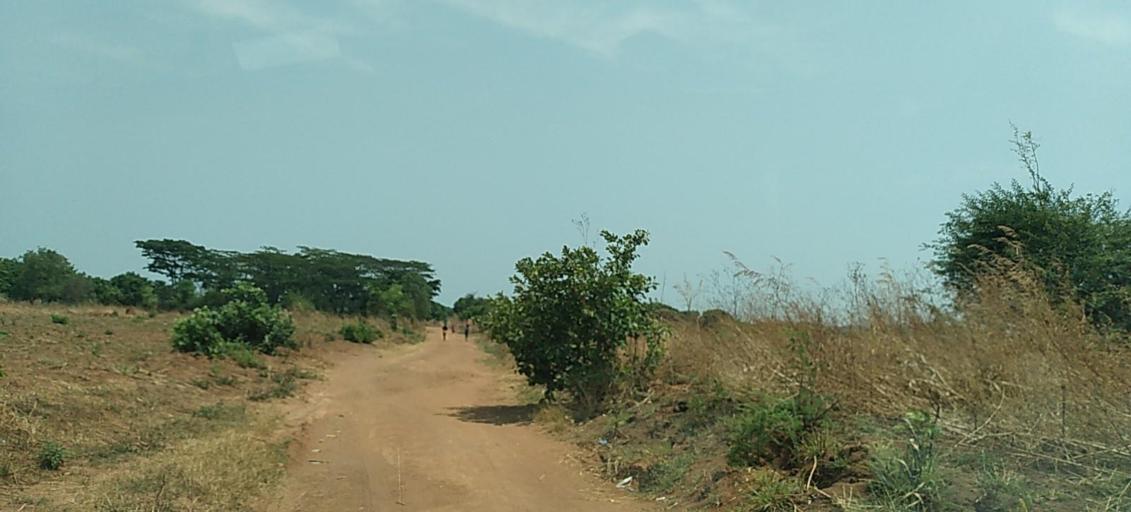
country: ZM
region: Copperbelt
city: Ndola
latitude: -13.0794
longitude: 28.7472
